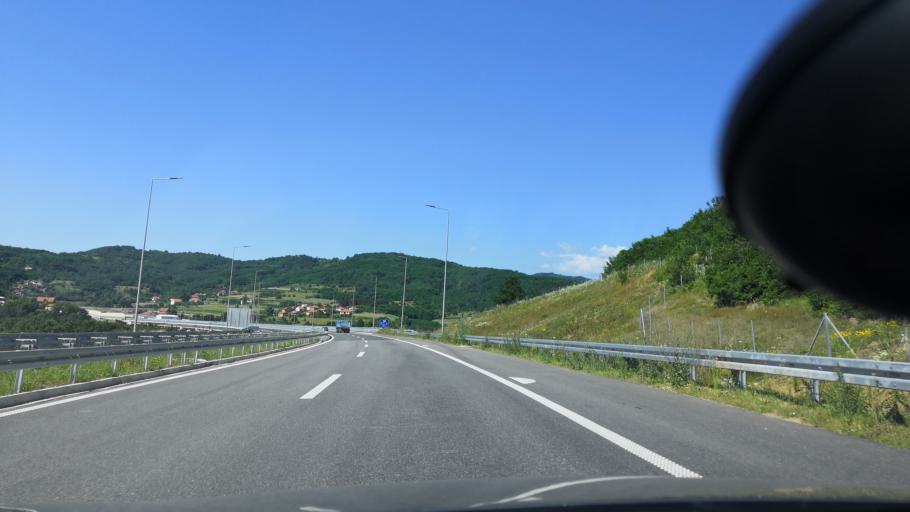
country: RS
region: Central Serbia
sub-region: Pcinjski Okrug
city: Vladicin Han
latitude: 42.7183
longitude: 22.0759
